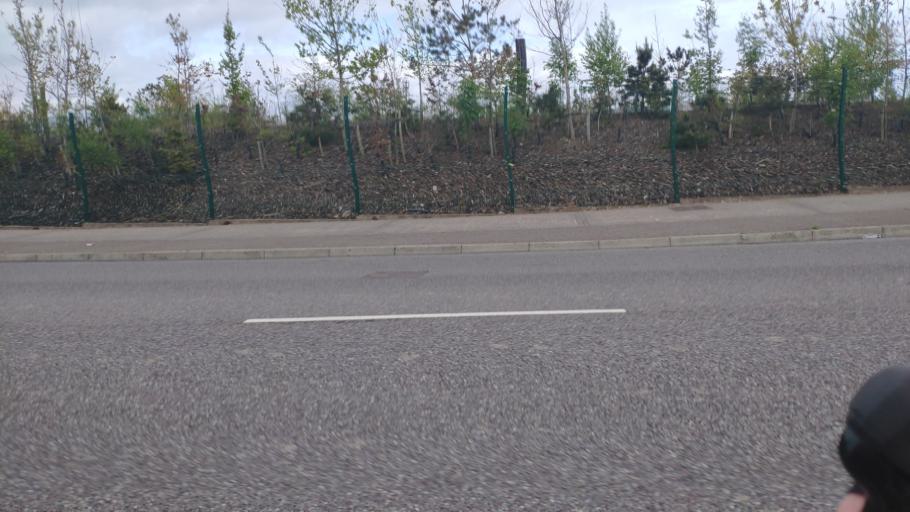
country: IE
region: Munster
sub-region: County Cork
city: Cork
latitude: 51.9065
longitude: -8.5186
